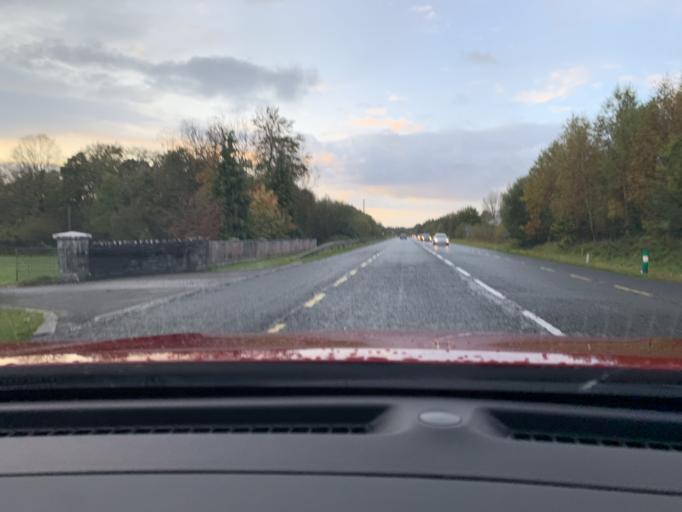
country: IE
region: Connaught
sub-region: County Leitrim
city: Carrick-on-Shannon
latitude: 53.9540
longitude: -8.1561
